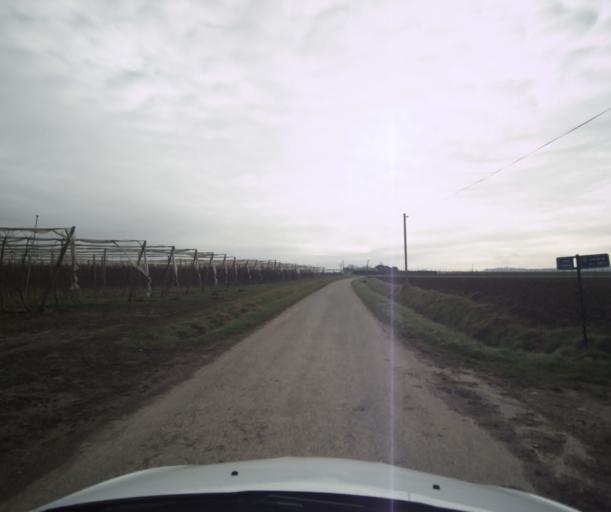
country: FR
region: Midi-Pyrenees
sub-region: Departement du Tarn-et-Garonne
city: Castelsarrasin
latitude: 44.0262
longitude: 1.1216
